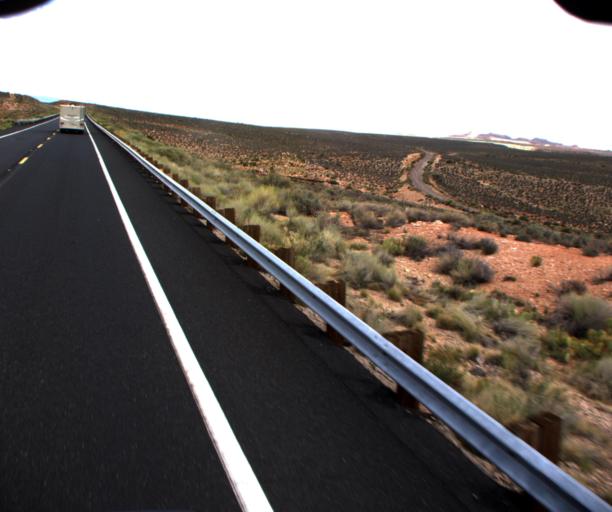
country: US
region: Arizona
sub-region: Coconino County
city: Tuba City
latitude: 35.9272
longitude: -111.6152
